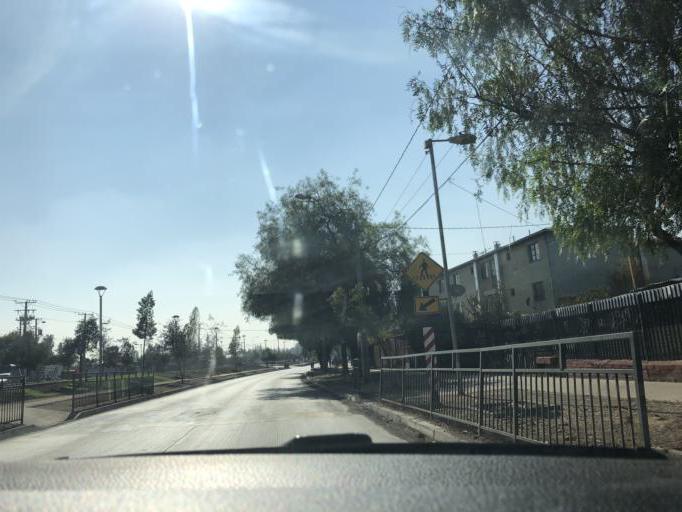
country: CL
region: Santiago Metropolitan
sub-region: Provincia de Santiago
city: La Pintana
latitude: -33.6266
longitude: -70.6283
